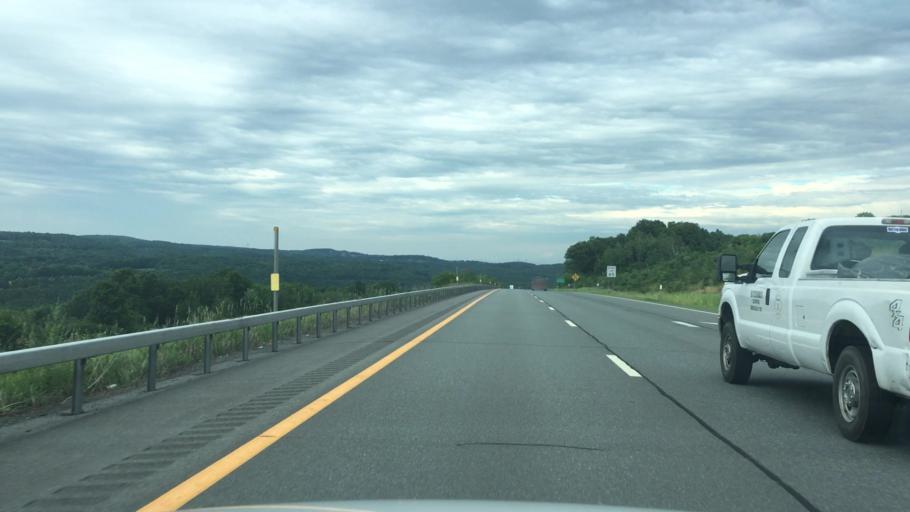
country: US
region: New York
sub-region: Albany County
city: Altamont
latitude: 42.7667
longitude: -74.1030
